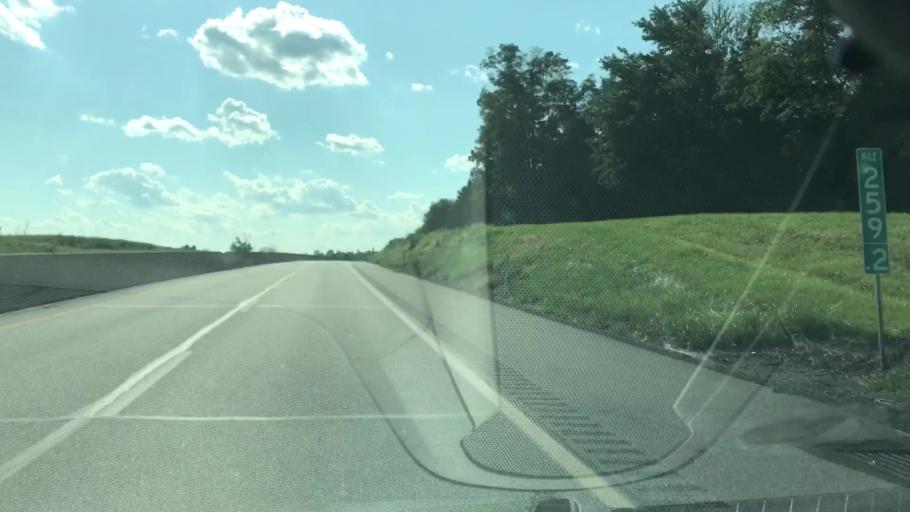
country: US
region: Pennsylvania
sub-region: Lancaster County
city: Elizabethtown
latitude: 40.2084
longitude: -76.5669
